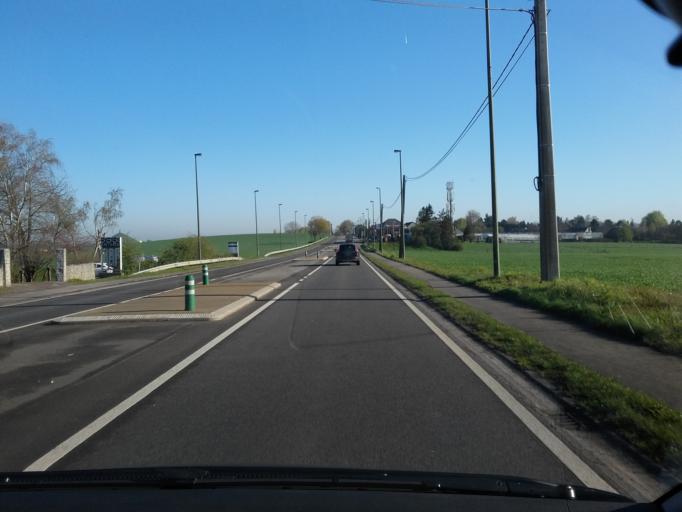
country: BE
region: Wallonia
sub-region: Province du Brabant Wallon
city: Braine-l'Alleud
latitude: 50.6596
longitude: 4.4131
